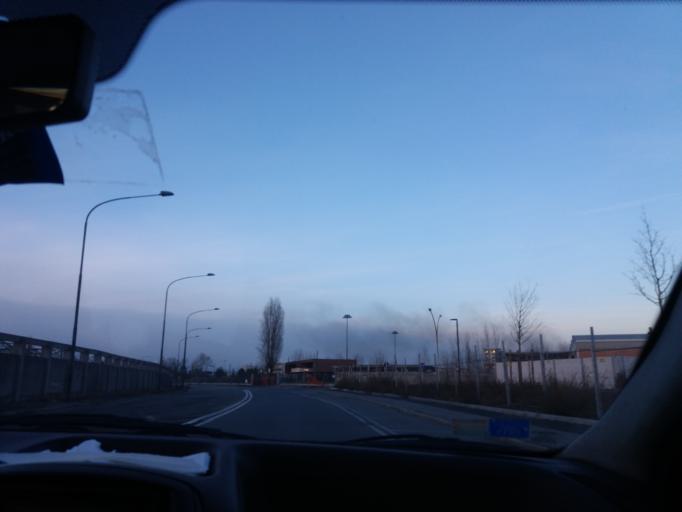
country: IT
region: Piedmont
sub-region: Provincia di Torino
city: Fornaci
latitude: 45.0276
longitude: 7.6090
